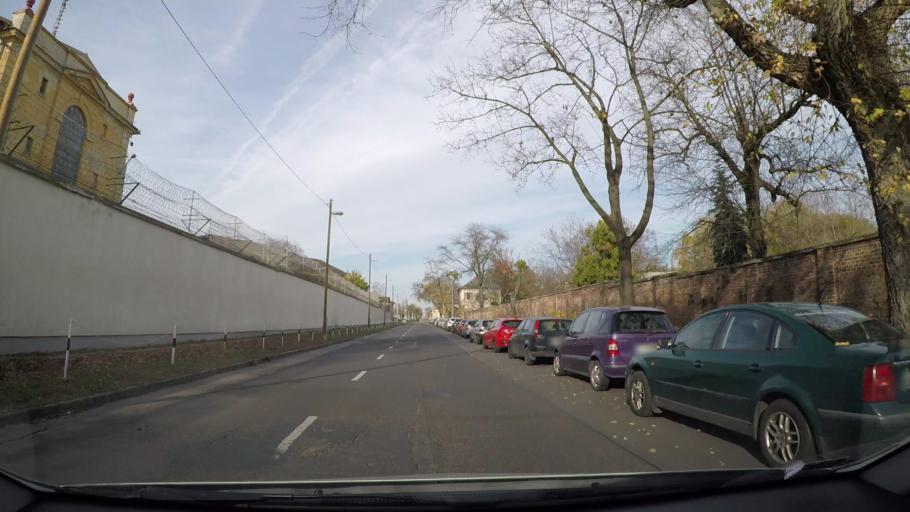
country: HU
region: Budapest
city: Budapest X. keruelet
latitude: 47.4705
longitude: 19.1785
